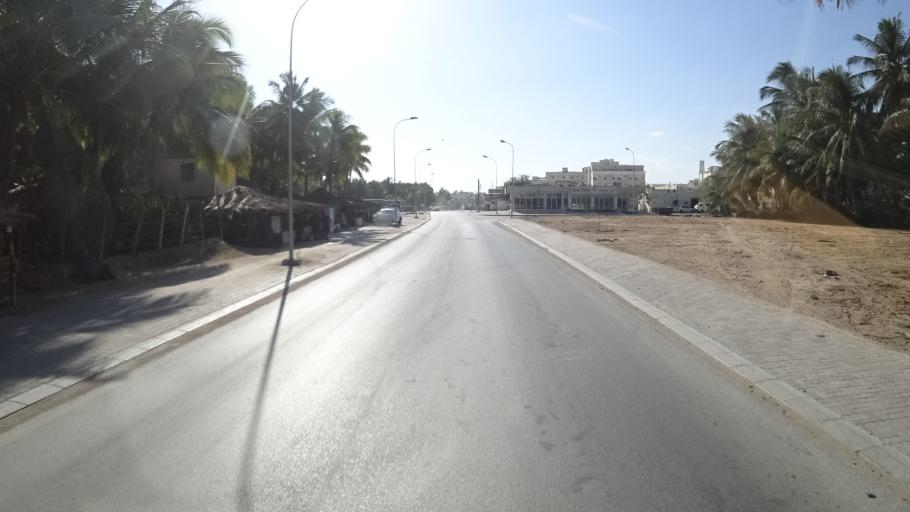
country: OM
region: Zufar
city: Salalah
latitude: 17.0103
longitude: 54.1035
